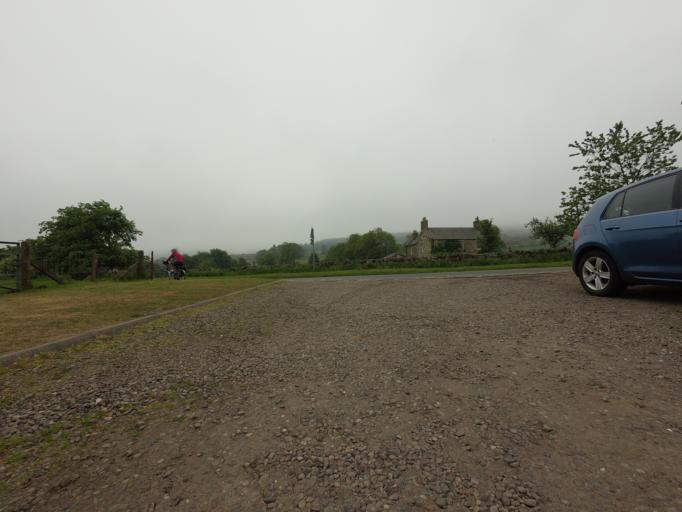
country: GB
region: Scotland
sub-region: Perth and Kinross
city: Kinross
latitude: 56.1667
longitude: -3.4583
